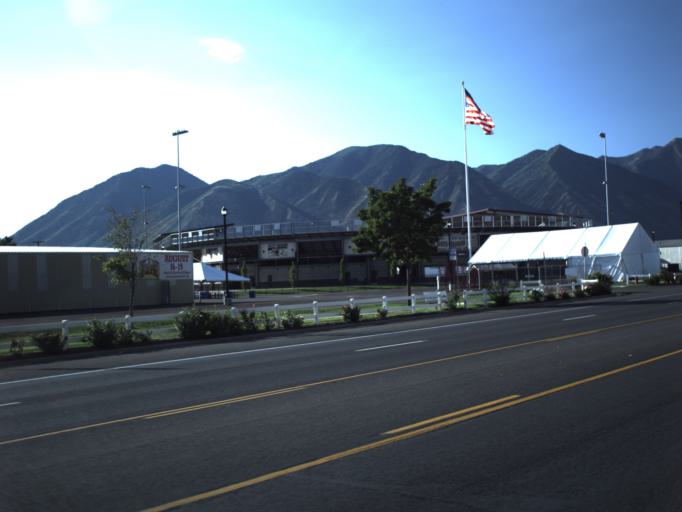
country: US
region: Utah
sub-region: Utah County
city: Spanish Fork
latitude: 40.1036
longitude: -111.6553
